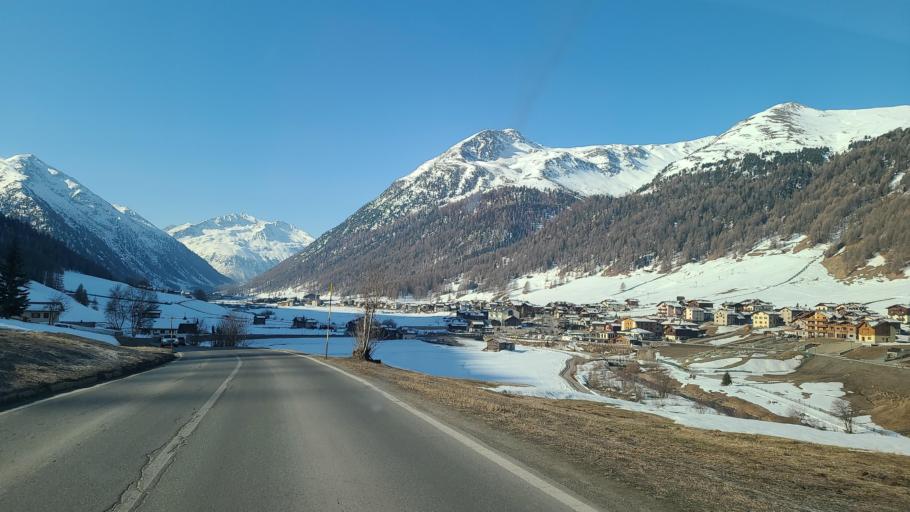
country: IT
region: Lombardy
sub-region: Provincia di Sondrio
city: Livigno
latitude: 46.5214
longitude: 10.1297
